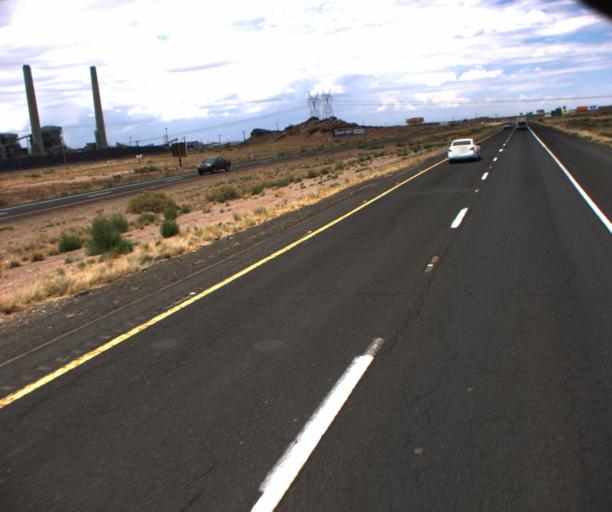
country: US
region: Arizona
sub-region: Navajo County
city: Joseph City
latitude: 34.9435
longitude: -110.2884
